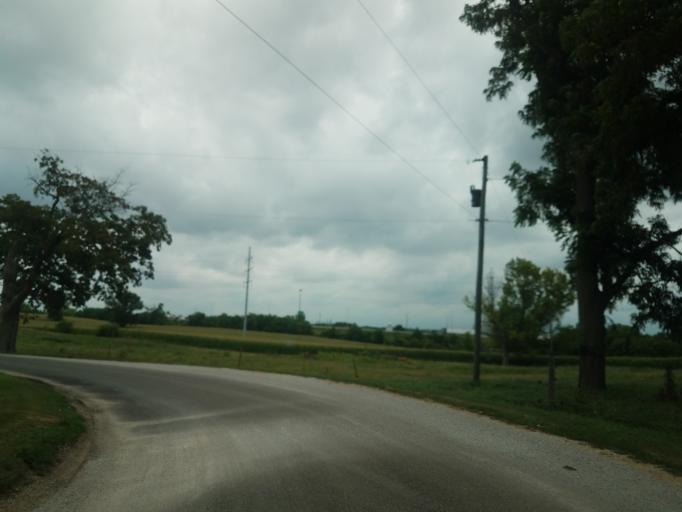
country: US
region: Illinois
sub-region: McLean County
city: Bloomington
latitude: 40.4747
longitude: -89.0330
